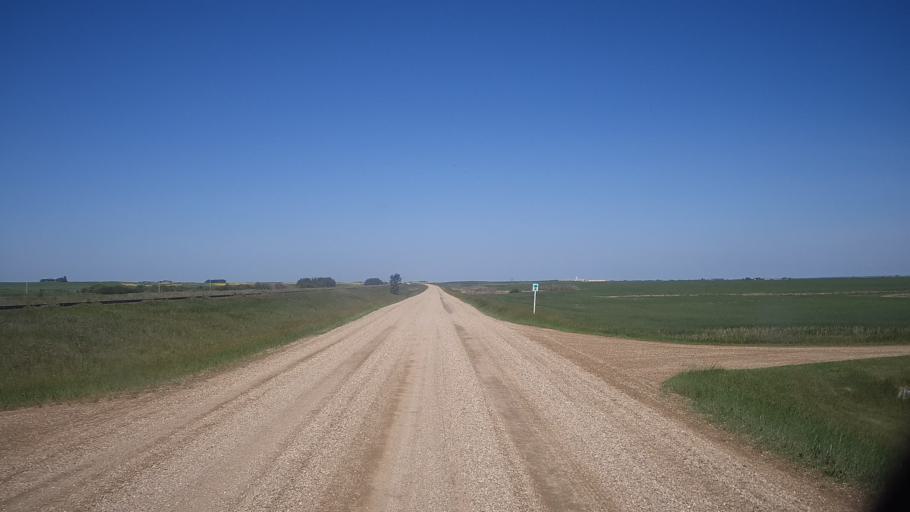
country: CA
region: Saskatchewan
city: Watrous
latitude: 51.8423
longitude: -105.9119
